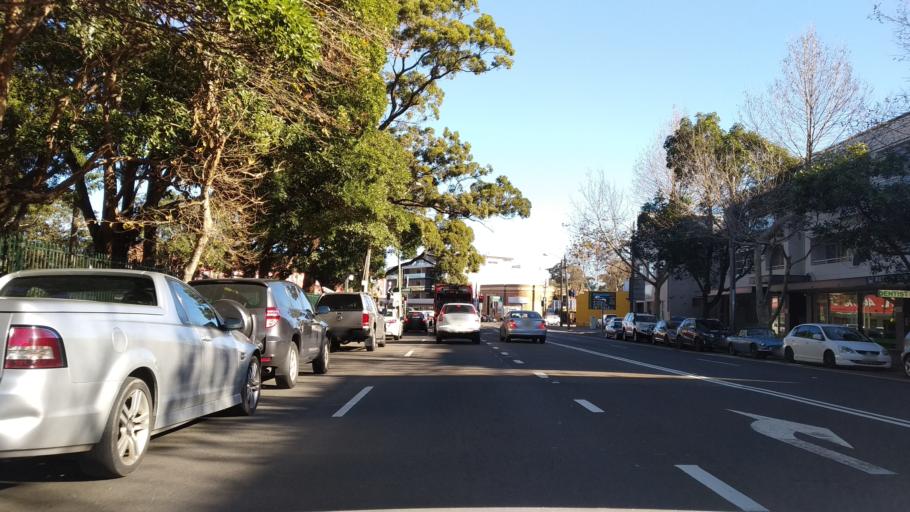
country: AU
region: New South Wales
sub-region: Botany Bay
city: Mascot
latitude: -33.9247
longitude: 151.1956
